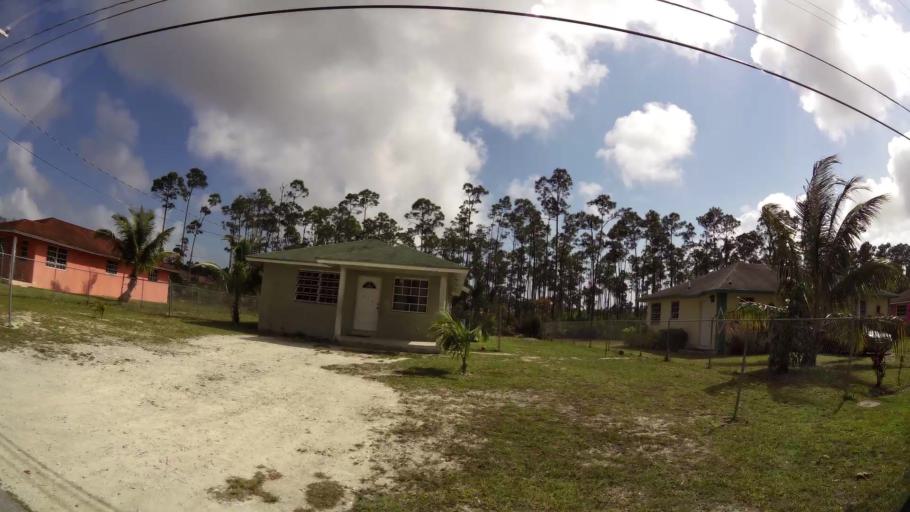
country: BS
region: Freeport
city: Freeport
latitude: 26.5265
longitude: -78.7138
